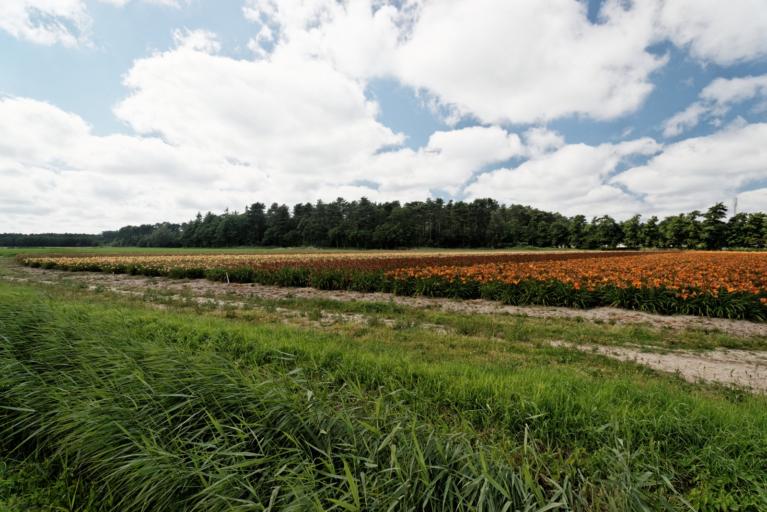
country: NL
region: North Holland
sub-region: Gemeente Texel
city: Den Burg
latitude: 53.0650
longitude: 4.7576
